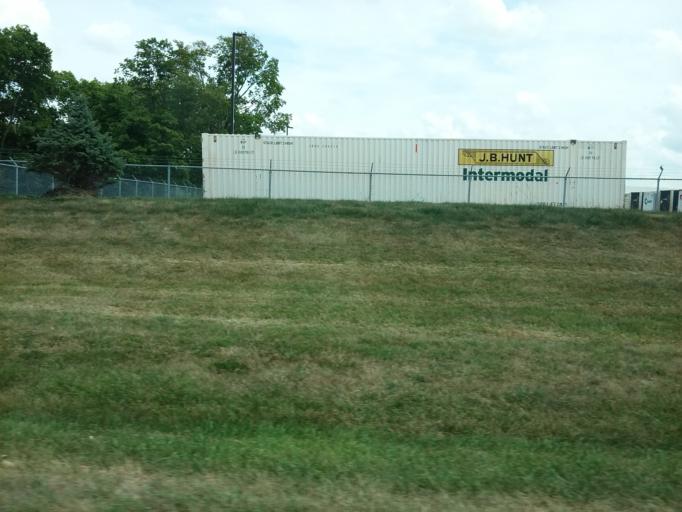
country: US
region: Ohio
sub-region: Hancock County
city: Findlay
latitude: 41.0553
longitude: -83.6885
